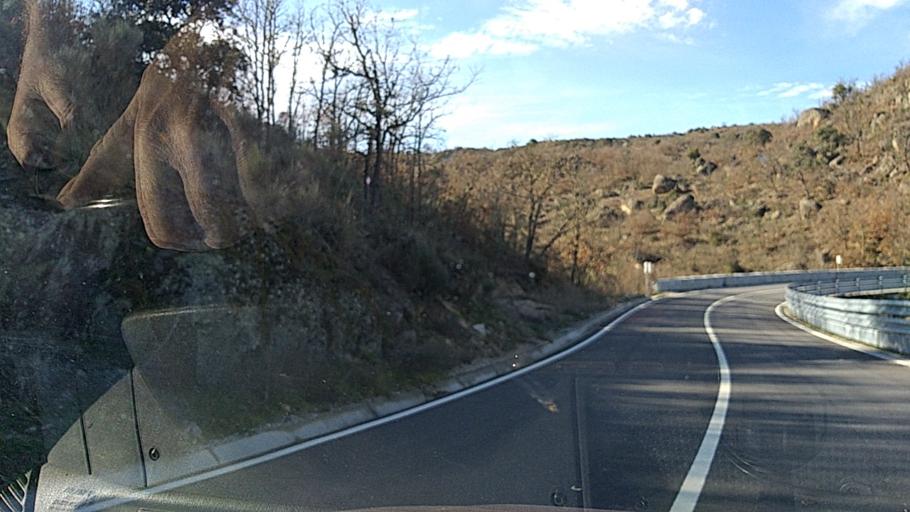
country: ES
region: Castille and Leon
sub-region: Provincia de Salamanca
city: Fuentes de Onoro
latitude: 40.6131
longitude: -6.9208
